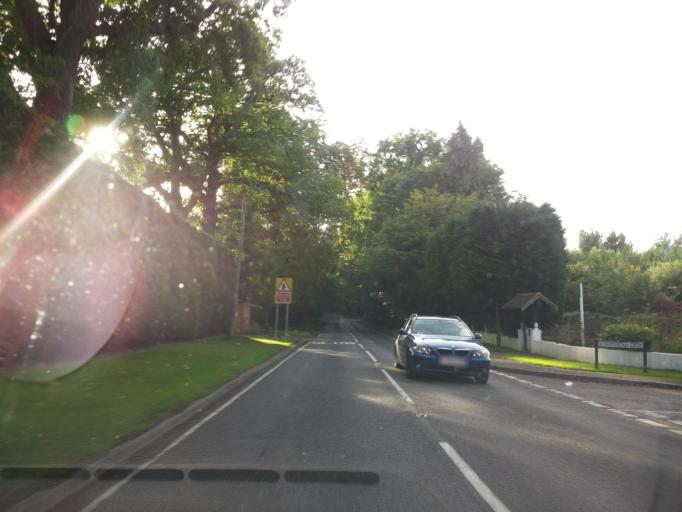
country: GB
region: England
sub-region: Surrey
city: Virginia Water
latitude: 51.3793
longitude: -0.5680
